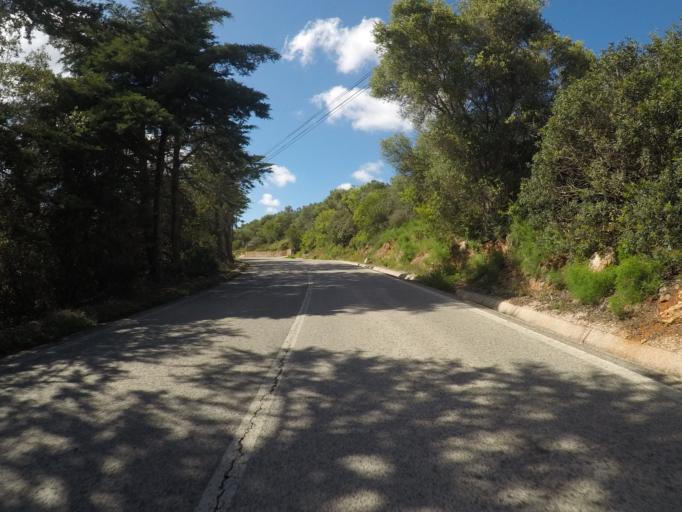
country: PT
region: Faro
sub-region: Vila do Bispo
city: Vila do Bispo
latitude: 37.0747
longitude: -8.8302
